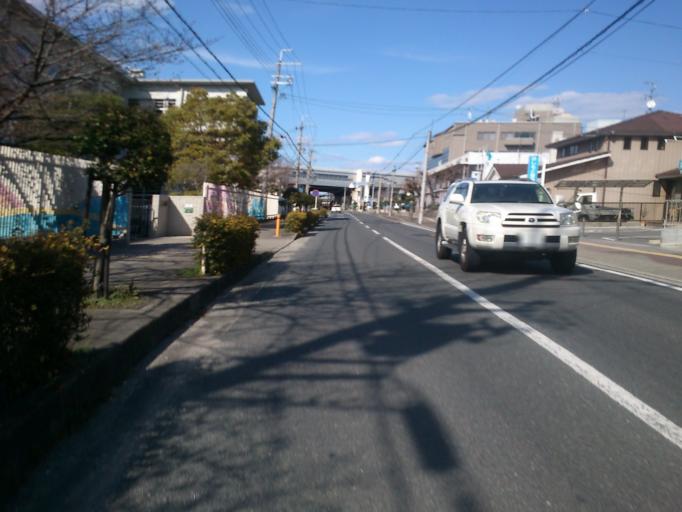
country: JP
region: Kyoto
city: Yawata
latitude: 34.9017
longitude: 135.6874
